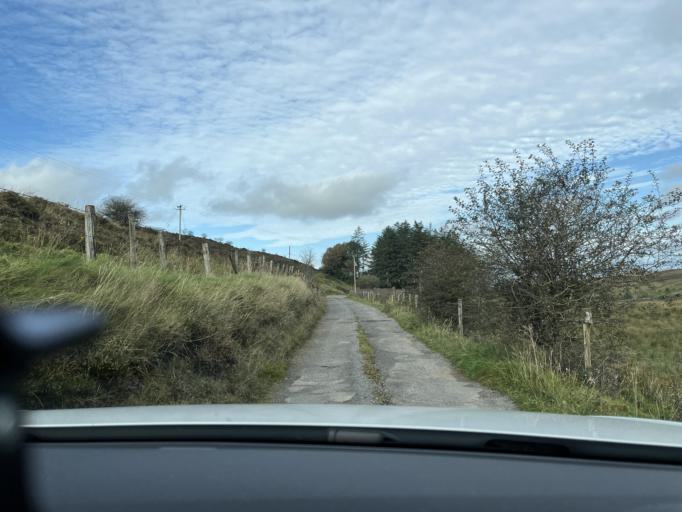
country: IE
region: Connaught
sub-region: Sligo
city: Ballymote
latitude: 54.0579
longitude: -8.4232
